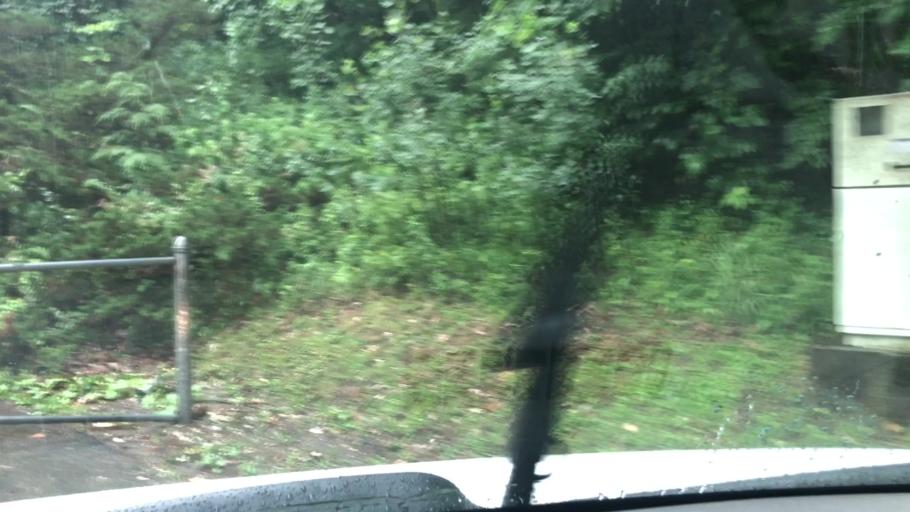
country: US
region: Massachusetts
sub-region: Berkshire County
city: Pittsfield
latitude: 42.4193
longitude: -73.2810
